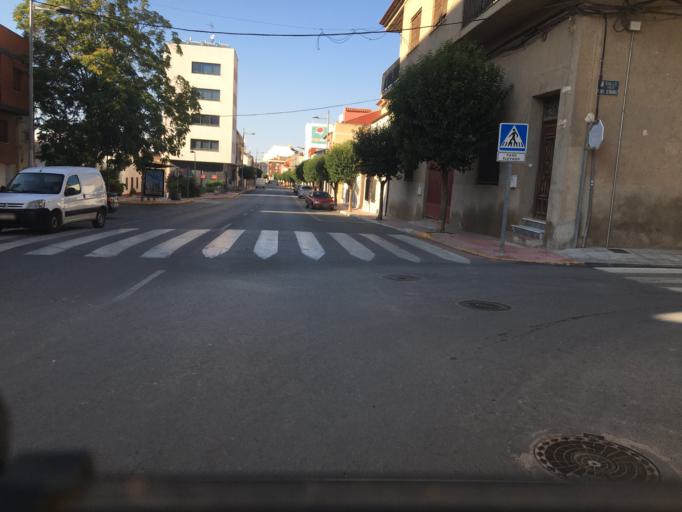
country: ES
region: Murcia
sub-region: Murcia
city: Puerto Lumbreras
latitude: 37.5571
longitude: -1.8119
